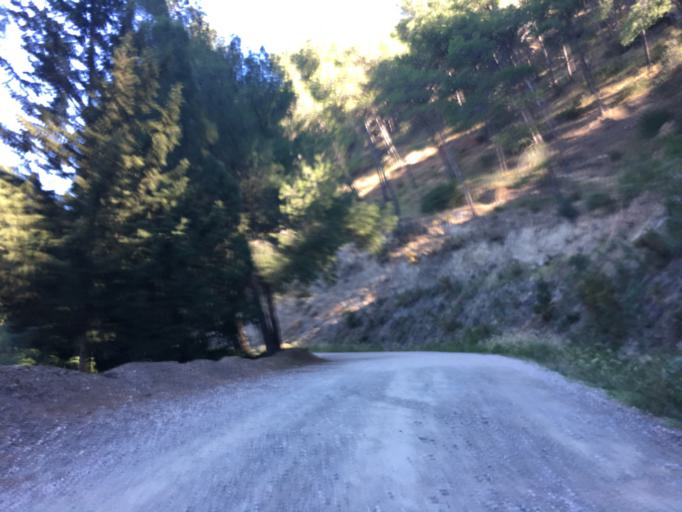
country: ES
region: Andalusia
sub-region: Provincia de Malaga
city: Malaga
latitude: 36.7741
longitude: -4.3847
